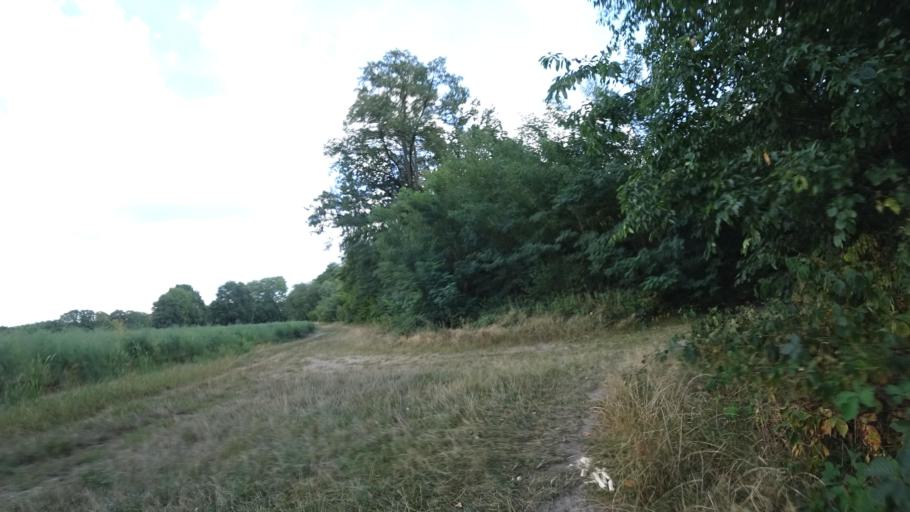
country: DE
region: North Rhine-Westphalia
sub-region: Regierungsbezirk Detmold
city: Verl
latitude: 51.9391
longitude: 8.4978
